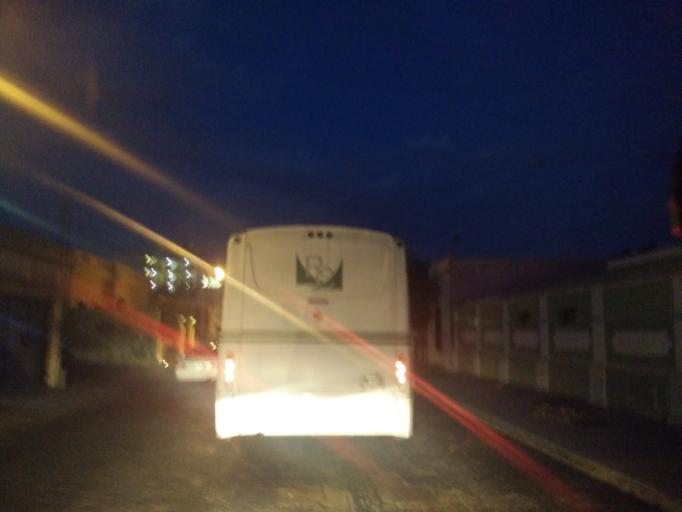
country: MX
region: Yucatan
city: Merida
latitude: 20.9706
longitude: -89.6354
